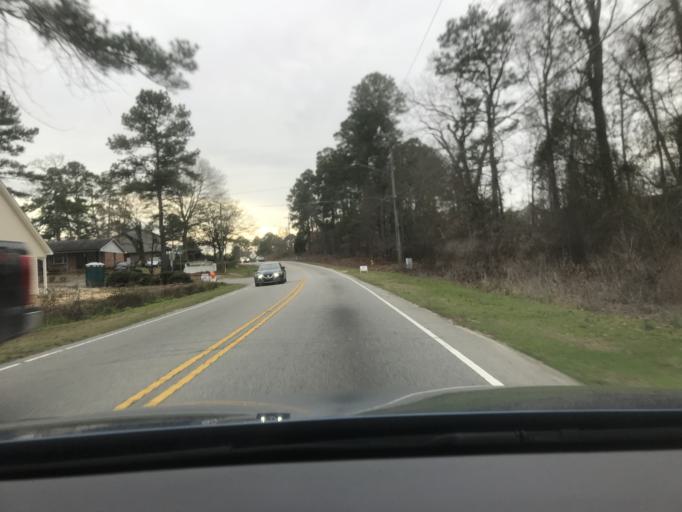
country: US
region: North Carolina
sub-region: Hoke County
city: Rockfish
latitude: 35.0290
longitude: -79.0008
